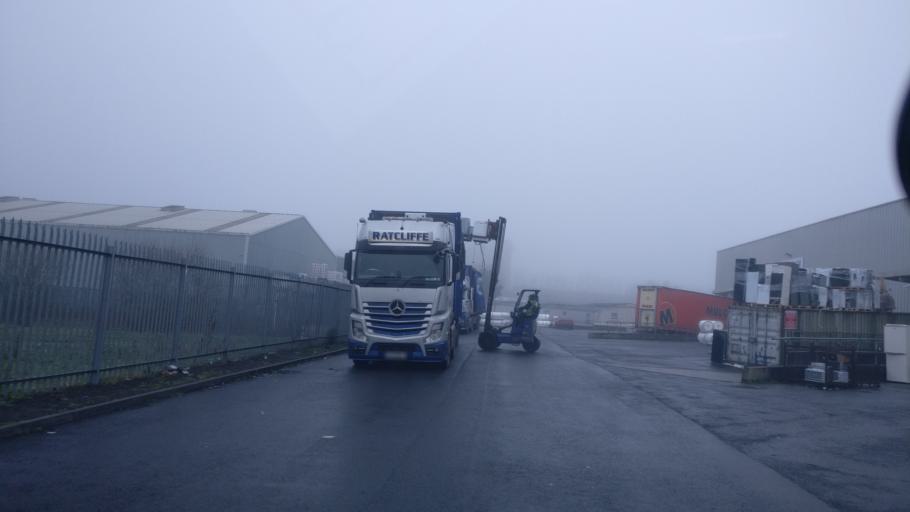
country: IE
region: Munster
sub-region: County Limerick
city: Luimneach
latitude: 52.6496
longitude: -8.5915
